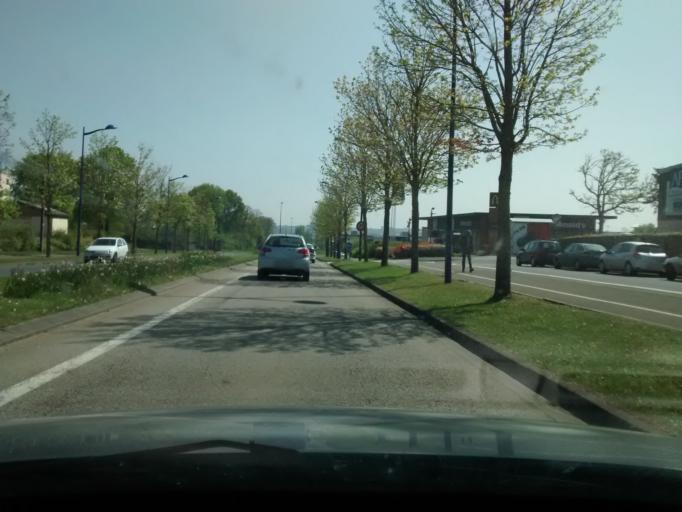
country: FR
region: Pays de la Loire
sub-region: Departement de la Sarthe
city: La Chapelle-Saint-Aubin
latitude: 48.0149
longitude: 0.1591
